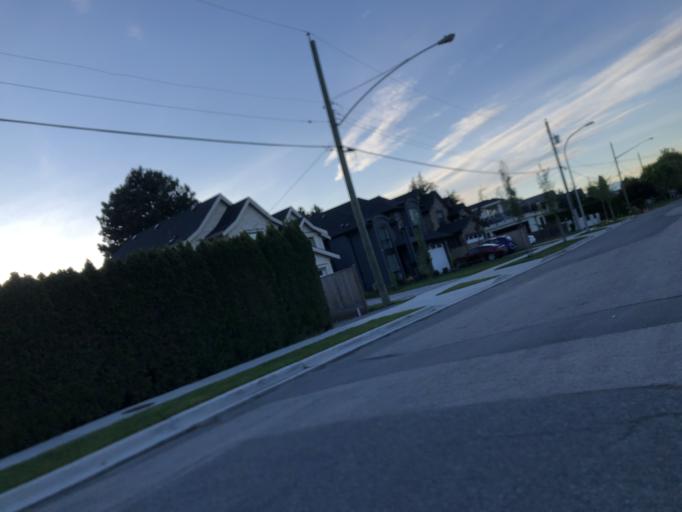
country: CA
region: British Columbia
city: Richmond
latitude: 49.1382
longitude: -123.1320
